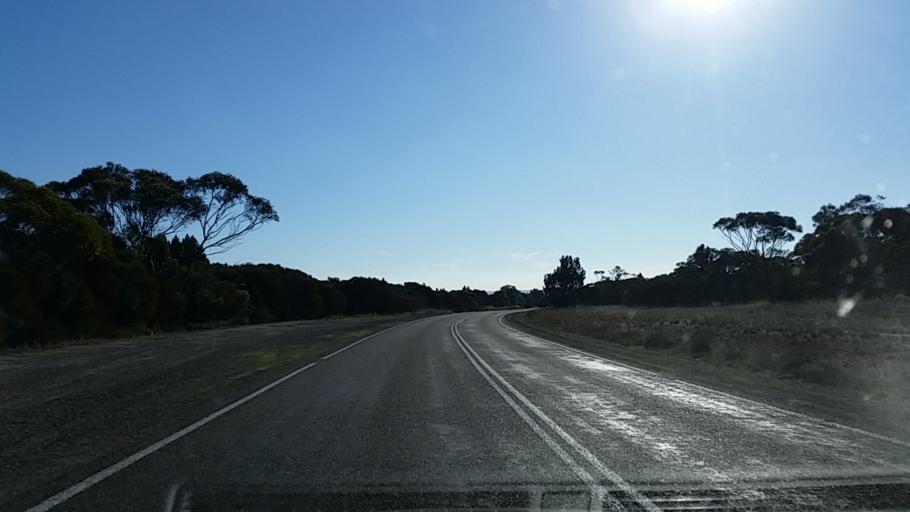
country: AU
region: South Australia
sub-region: Murray Bridge
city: Murray Bridge
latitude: -35.1334
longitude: 139.1978
